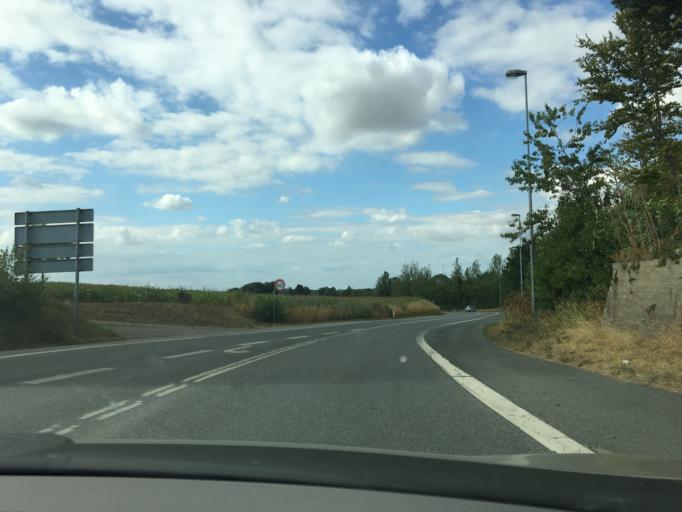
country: DK
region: South Denmark
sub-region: Odense Kommune
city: Bellinge
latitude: 55.3905
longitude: 10.2618
